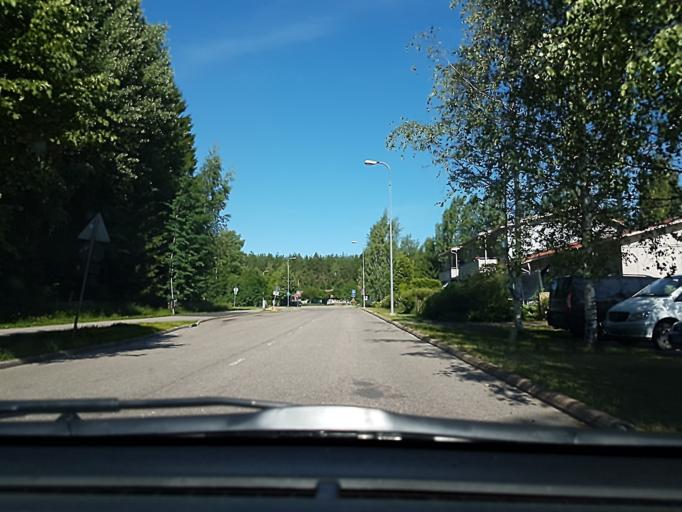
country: FI
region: Uusimaa
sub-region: Helsinki
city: Vantaa
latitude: 60.3361
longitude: 25.0580
